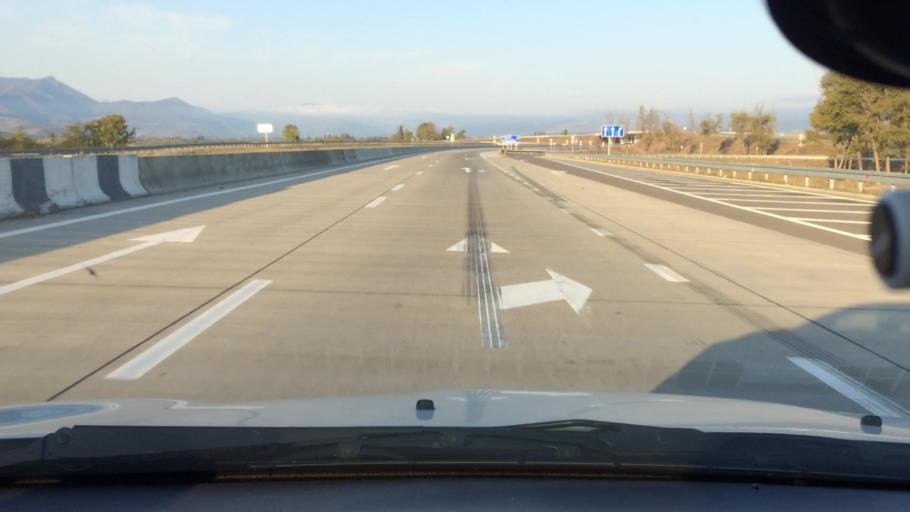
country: GE
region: Shida Kartli
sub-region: Khashuris Raioni
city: Khashuri
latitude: 42.0111
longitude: 43.7066
